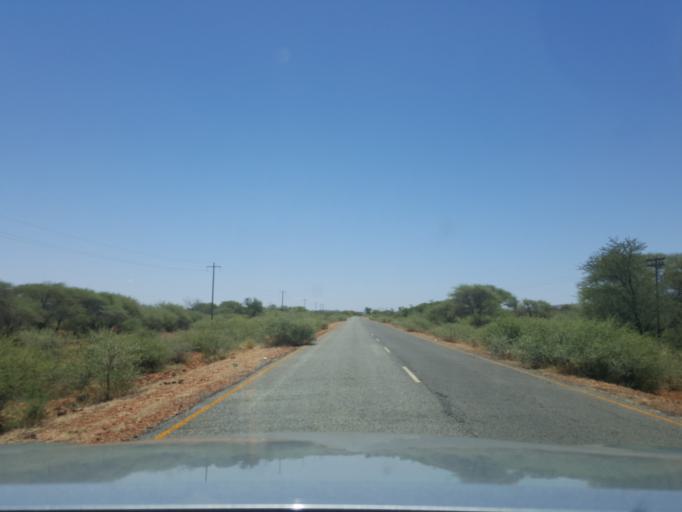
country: BW
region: South East
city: Ramotswa
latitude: -24.8806
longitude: 25.8906
